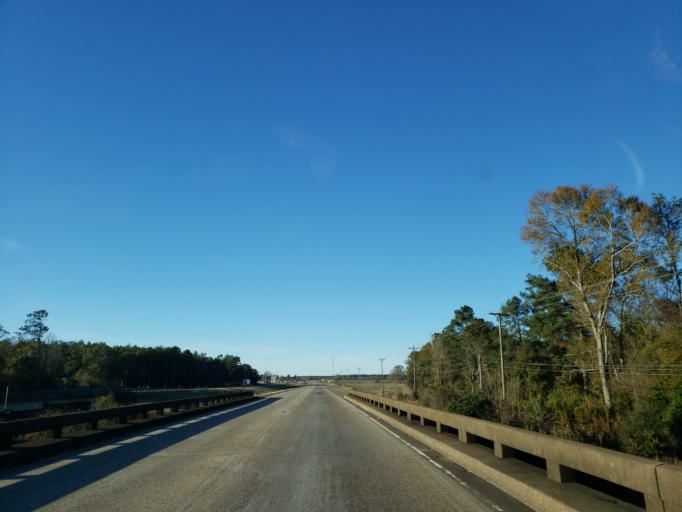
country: US
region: Mississippi
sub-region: Forrest County
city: Rawls Springs
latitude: 31.4256
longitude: -89.4143
